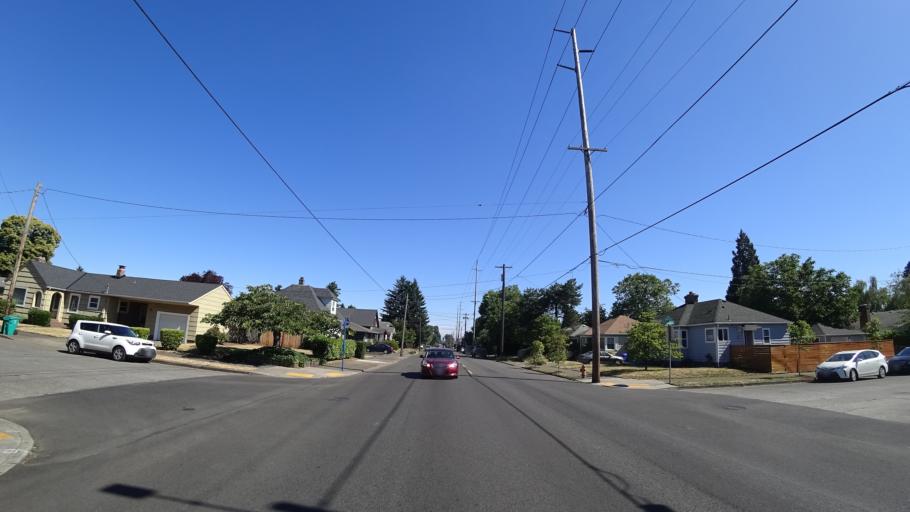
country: US
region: Oregon
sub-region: Multnomah County
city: Portland
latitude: 45.5681
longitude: -122.6956
